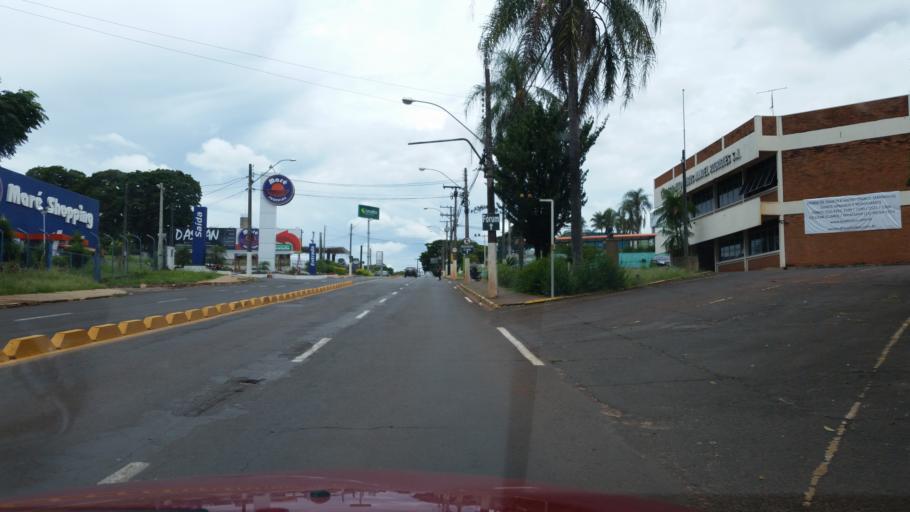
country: BR
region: Sao Paulo
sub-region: Avare
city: Avare
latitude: -23.0964
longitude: -48.9377
